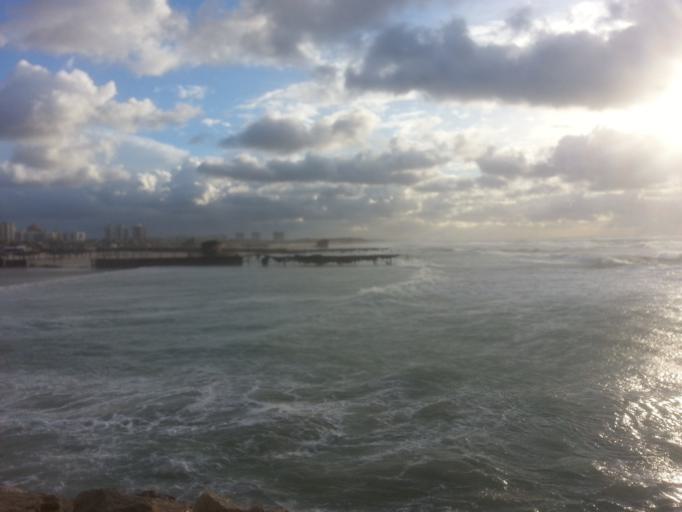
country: IL
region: Southern District
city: Ashdod
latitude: 31.7927
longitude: 34.6270
